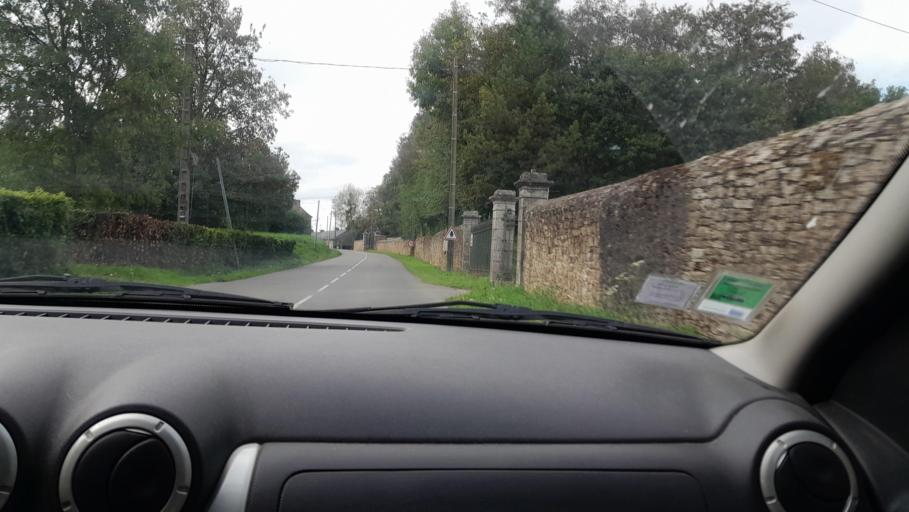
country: FR
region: Brittany
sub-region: Departement d'Ille-et-Vilaine
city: Le Pertre
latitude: 48.0373
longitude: -1.0430
